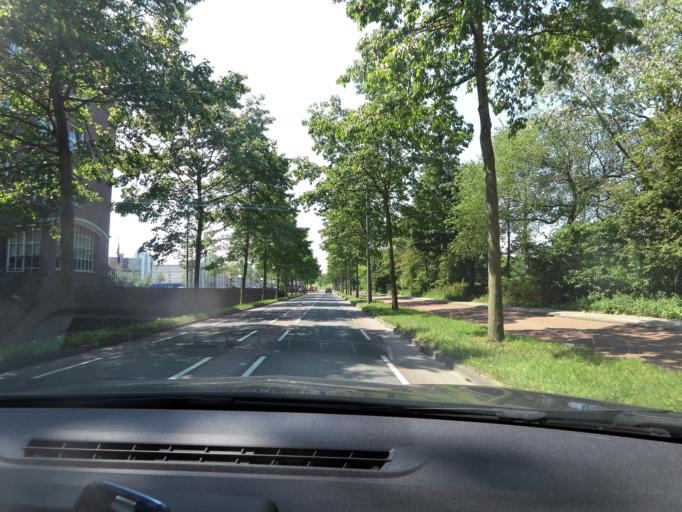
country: NL
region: South Holland
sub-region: Gemeente Rotterdam
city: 's-Gravenland
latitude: 51.9090
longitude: 4.5298
